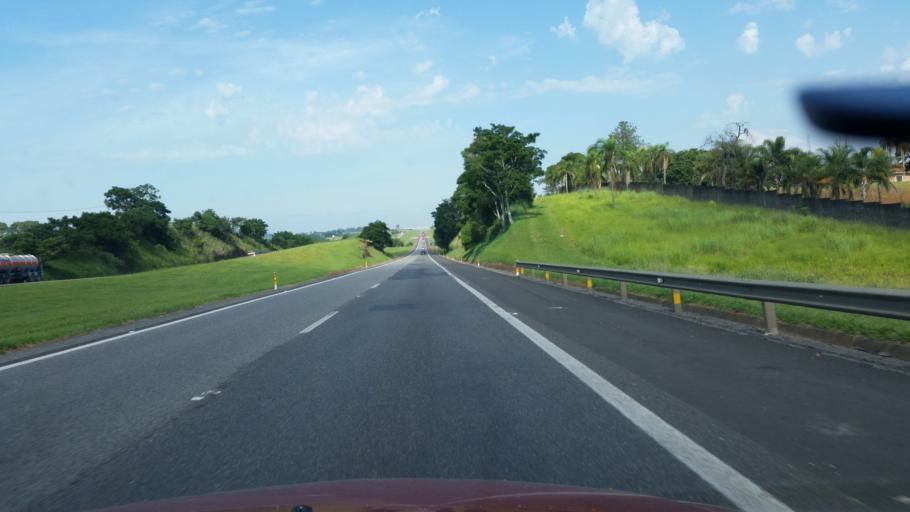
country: BR
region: Sao Paulo
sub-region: Tatui
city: Tatui
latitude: -23.2587
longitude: -47.8649
